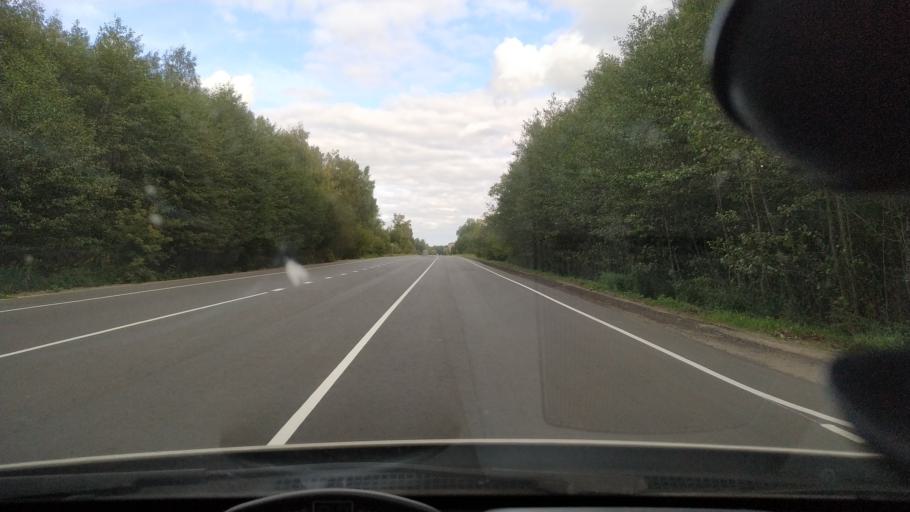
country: RU
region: Moskovskaya
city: Kabanovo
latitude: 55.7366
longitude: 38.9250
